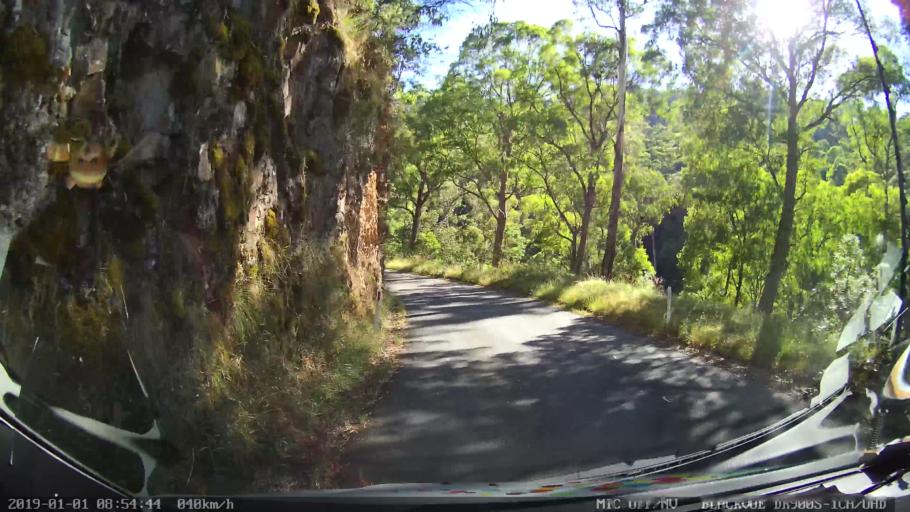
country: AU
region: New South Wales
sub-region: Snowy River
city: Jindabyne
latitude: -36.2585
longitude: 148.1932
